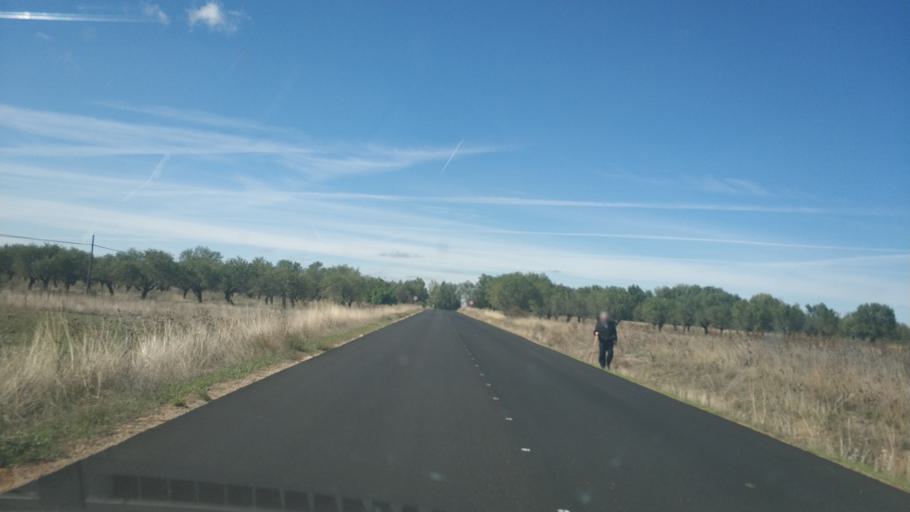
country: ES
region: Castille and Leon
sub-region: Provincia de Burgos
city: Puentedura
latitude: 42.0328
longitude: -3.6393
